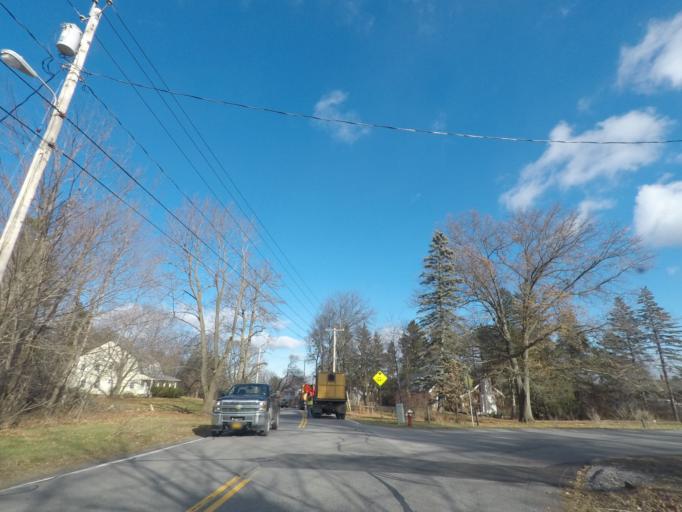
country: US
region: New York
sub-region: Schenectady County
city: Schenectady
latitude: 42.8127
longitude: -73.8882
